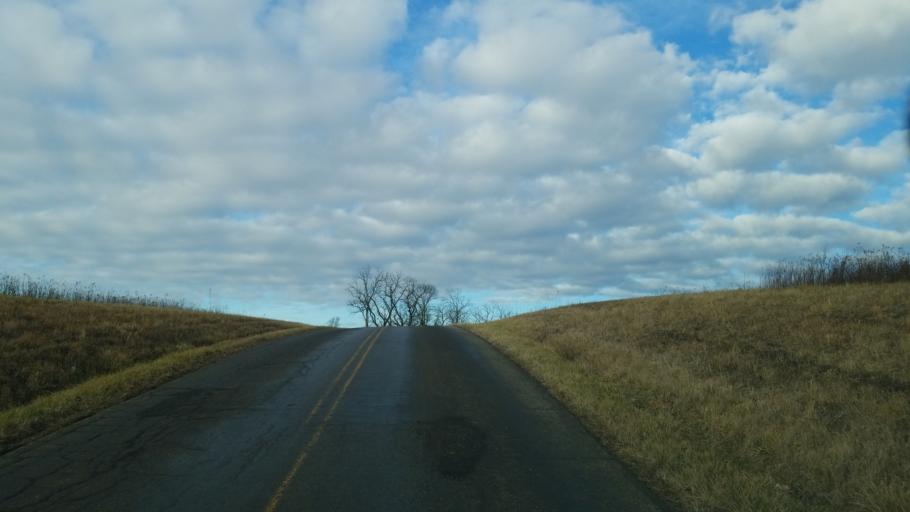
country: US
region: Ohio
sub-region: Knox County
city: Oak Hill
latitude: 40.3146
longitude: -82.2886
